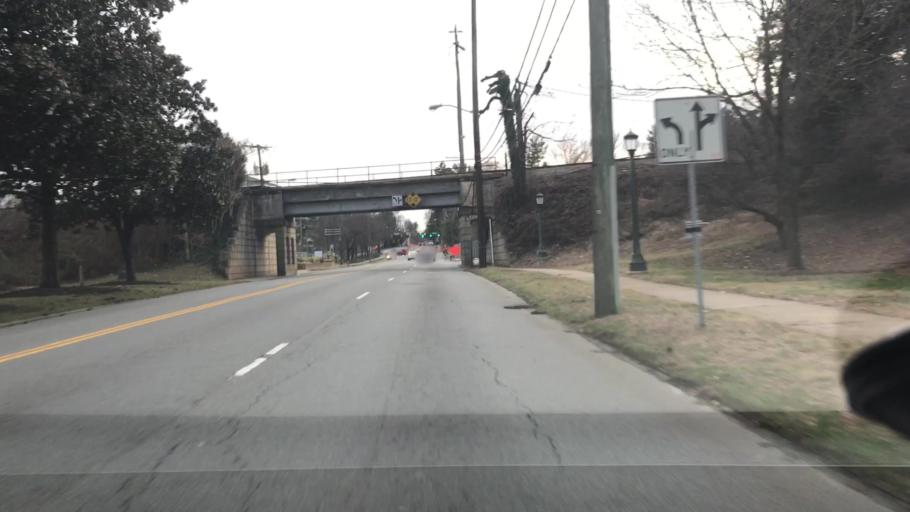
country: US
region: Virginia
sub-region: City of Charlottesville
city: Charlottesville
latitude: 38.0420
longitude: -78.5060
